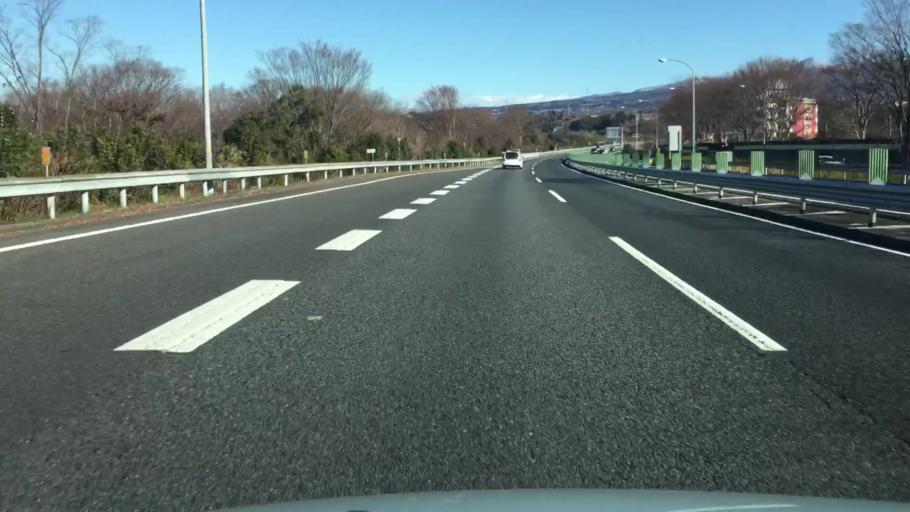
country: JP
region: Gunma
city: Shibukawa
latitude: 36.4768
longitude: 139.0165
